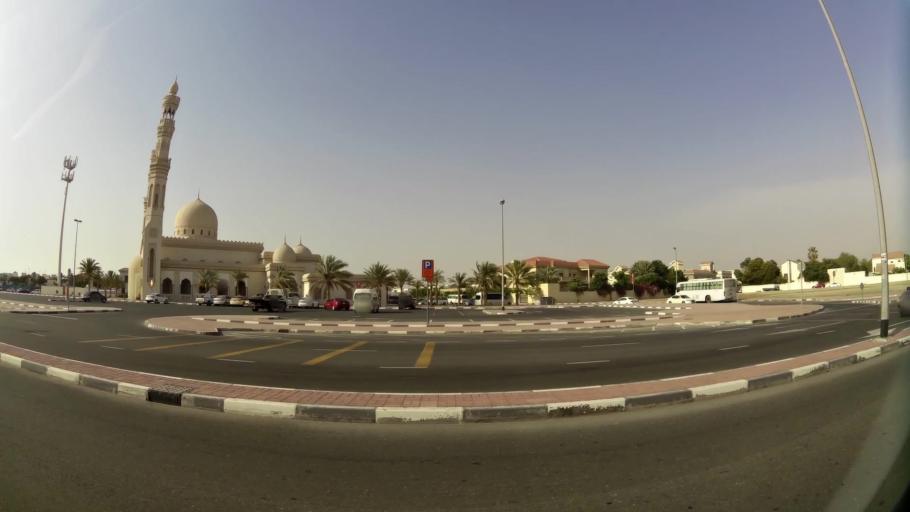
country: AE
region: Ash Shariqah
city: Sharjah
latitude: 25.2370
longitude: 55.3515
